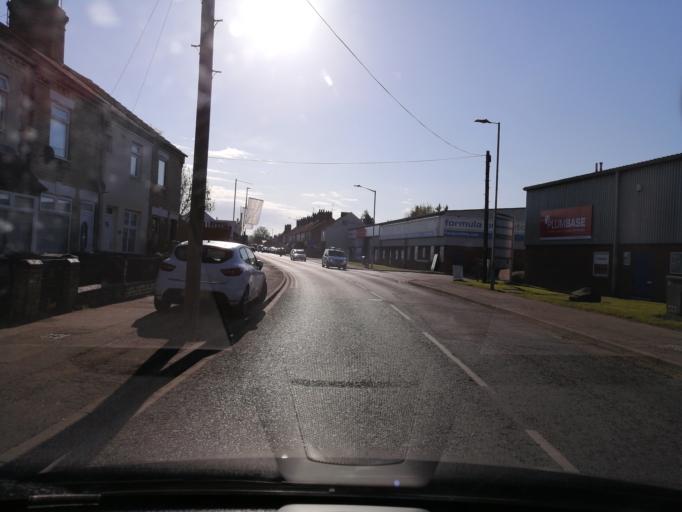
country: GB
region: England
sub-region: Peterborough
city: Peterborough
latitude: 52.5710
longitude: -0.2258
